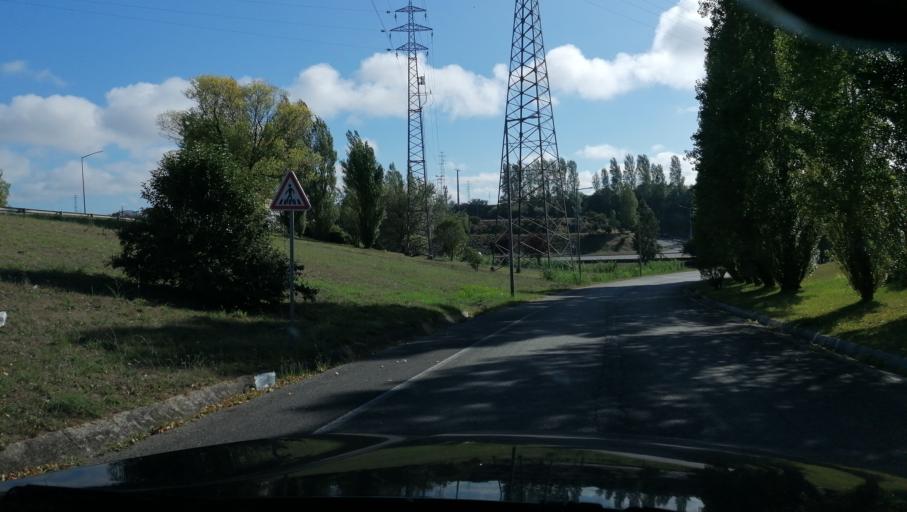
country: PT
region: Aveiro
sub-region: Aveiro
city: Aveiro
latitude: 40.6370
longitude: -8.6353
